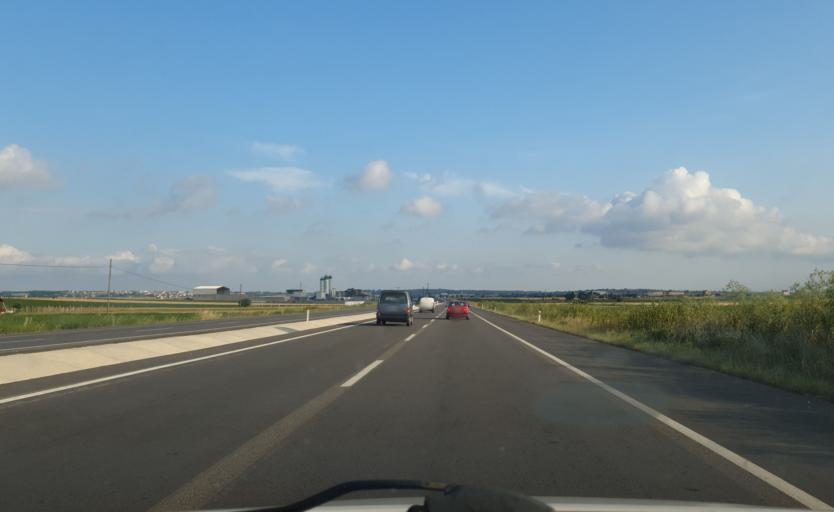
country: TR
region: Tekirdag
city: Saray
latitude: 41.4026
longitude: 27.9232
